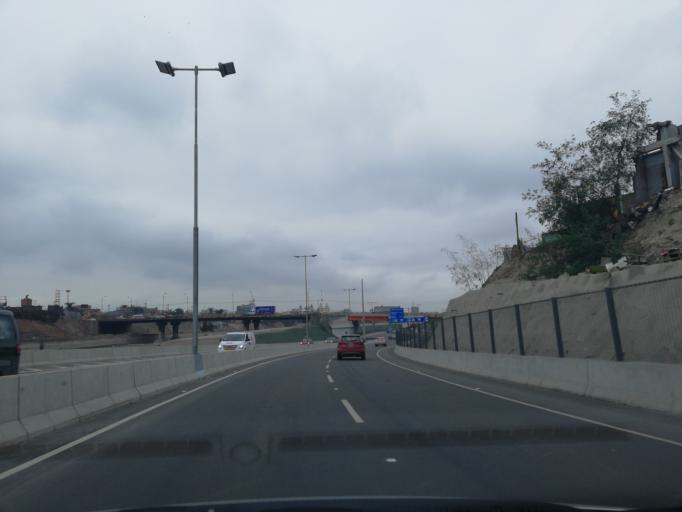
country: PE
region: Lima
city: Lima
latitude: -12.0433
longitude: -77.0175
